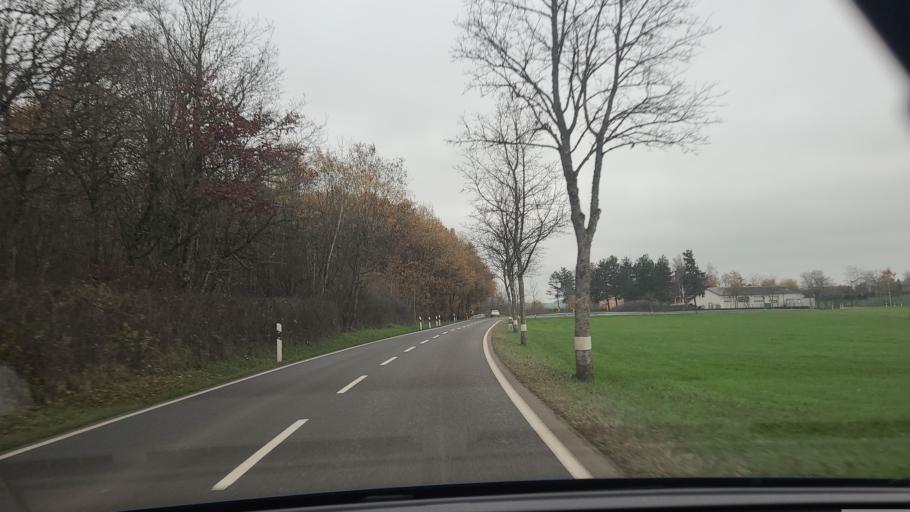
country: LU
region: Luxembourg
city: Schouweiler
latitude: 49.5936
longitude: 5.9443
